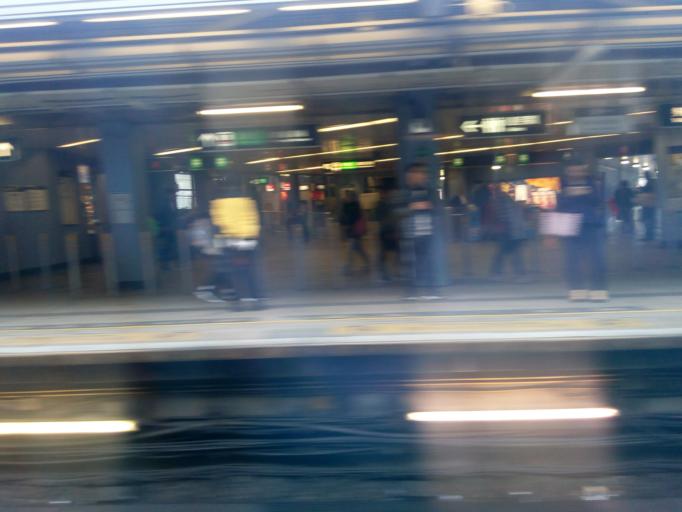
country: HK
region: Wong Tai Sin
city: Wong Tai Sin
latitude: 22.3371
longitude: 114.1758
